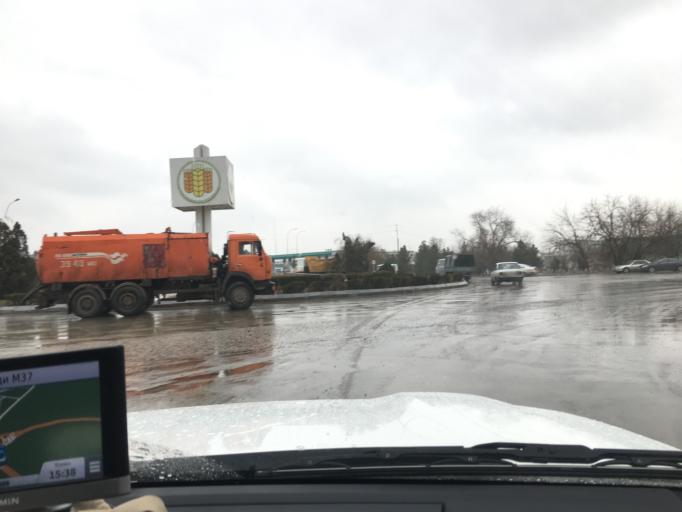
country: TM
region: Mary
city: Mary
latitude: 37.5718
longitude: 61.8333
